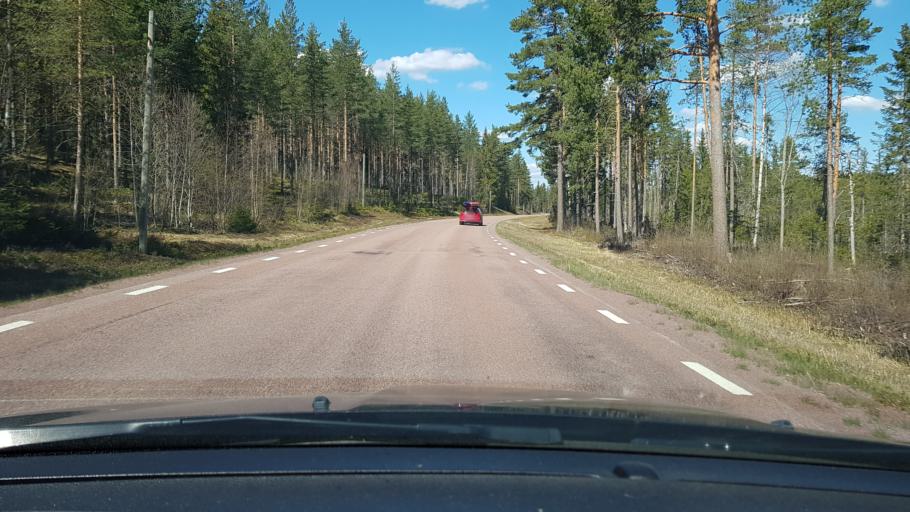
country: SE
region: Dalarna
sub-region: Alvdalens Kommun
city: AElvdalen
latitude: 61.1150
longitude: 14.1004
